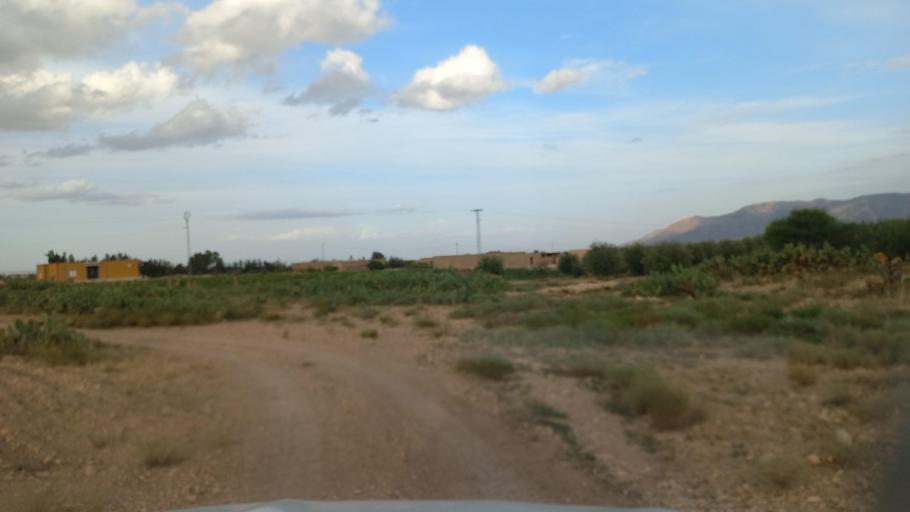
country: TN
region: Al Qasrayn
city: Sbiba
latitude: 35.4394
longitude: 9.0908
